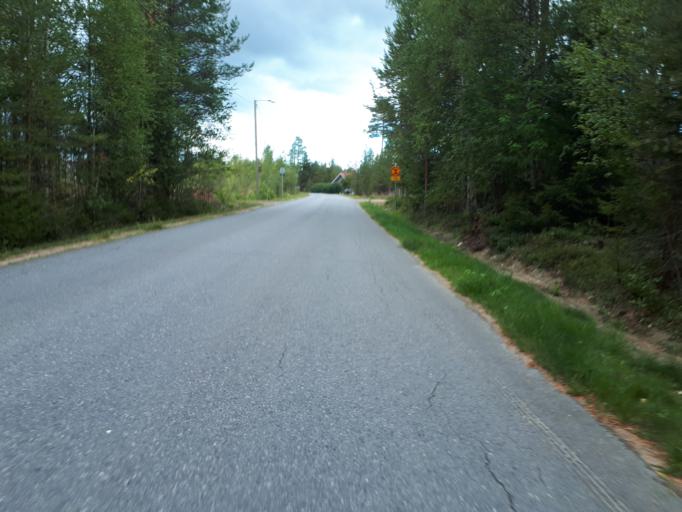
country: FI
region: Northern Ostrobothnia
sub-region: Oulunkaari
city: Ii
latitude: 65.3249
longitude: 25.3963
